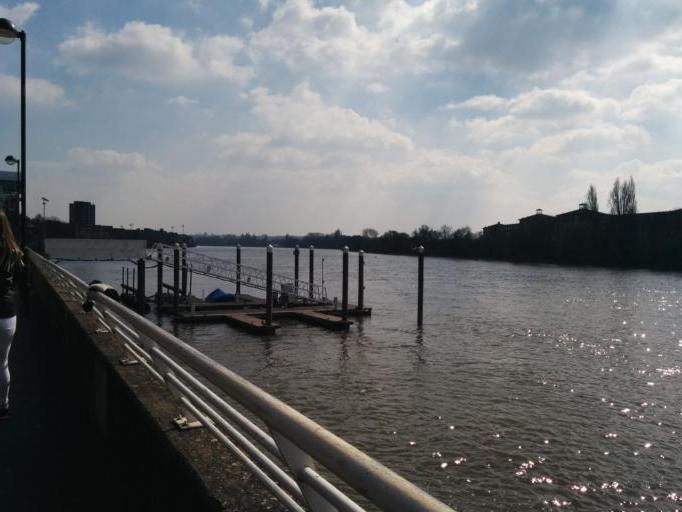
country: GB
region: England
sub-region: Greater London
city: Hammersmith
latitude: 51.4856
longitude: -0.2260
